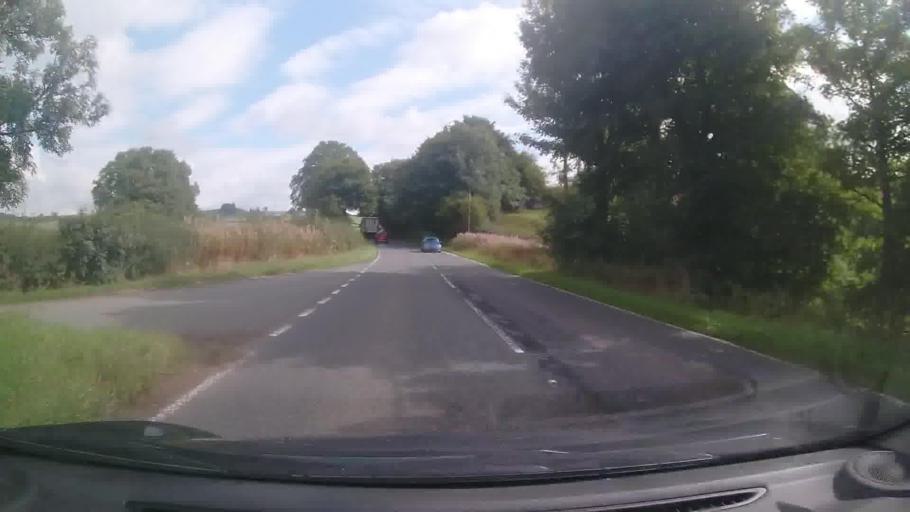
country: GB
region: Wales
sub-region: Sir Powys
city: Mochdre
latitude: 52.4797
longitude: -3.3348
